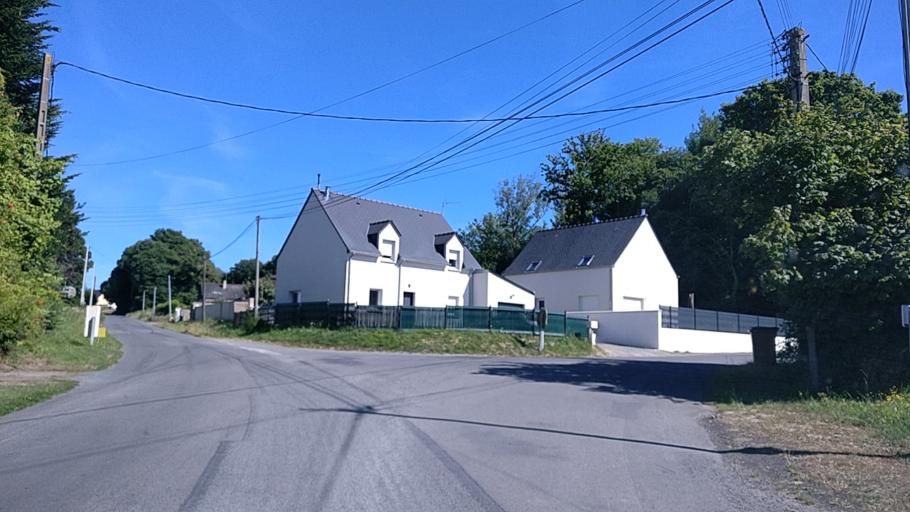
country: FR
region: Brittany
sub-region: Departement d'Ille-et-Vilaine
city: Plerguer
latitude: 48.5272
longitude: -1.8606
